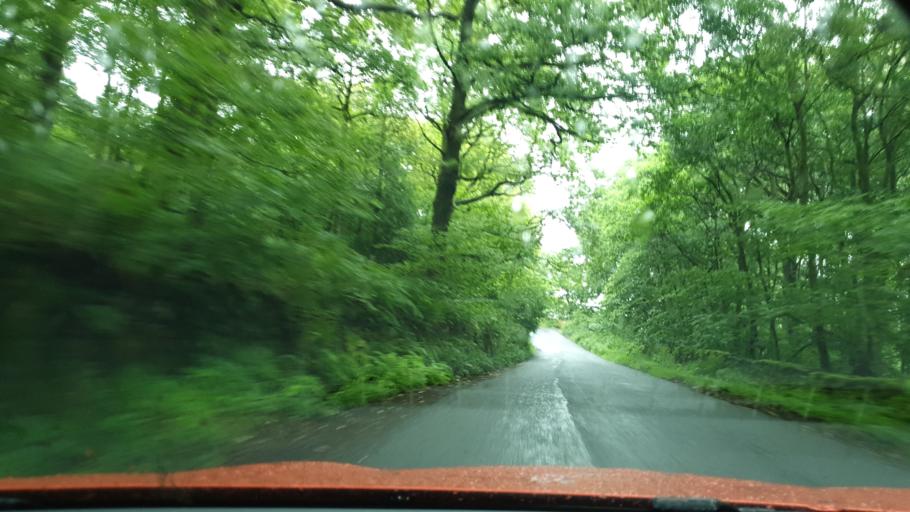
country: GB
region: England
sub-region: Cumbria
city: Millom
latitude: 54.3331
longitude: -3.2356
